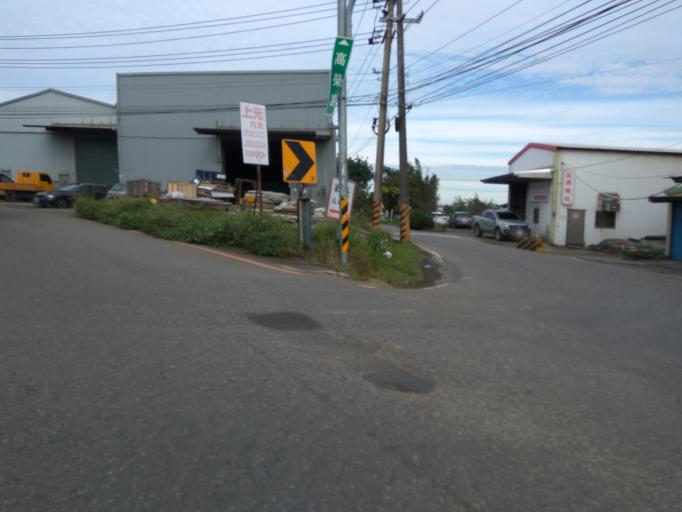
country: TW
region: Taiwan
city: Daxi
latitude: 24.9415
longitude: 121.1578
